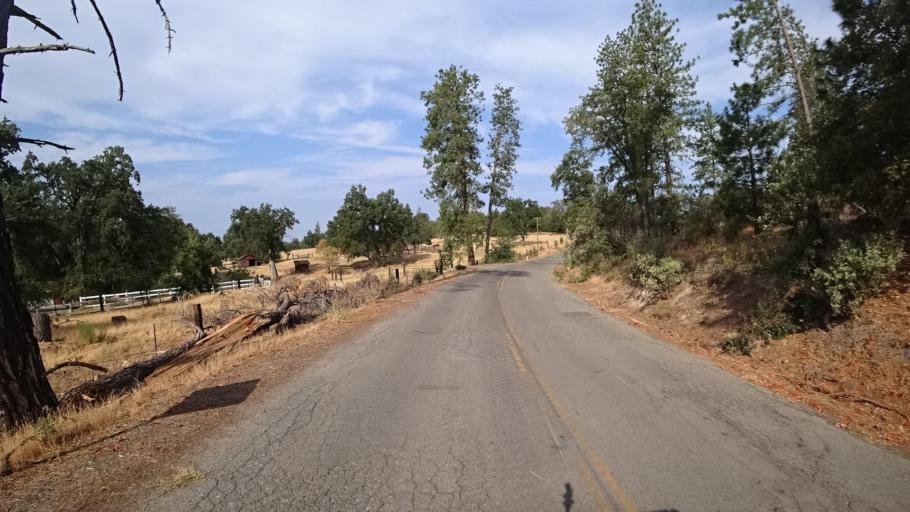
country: US
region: California
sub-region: Mariposa County
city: Midpines
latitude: 37.5003
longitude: -119.8078
